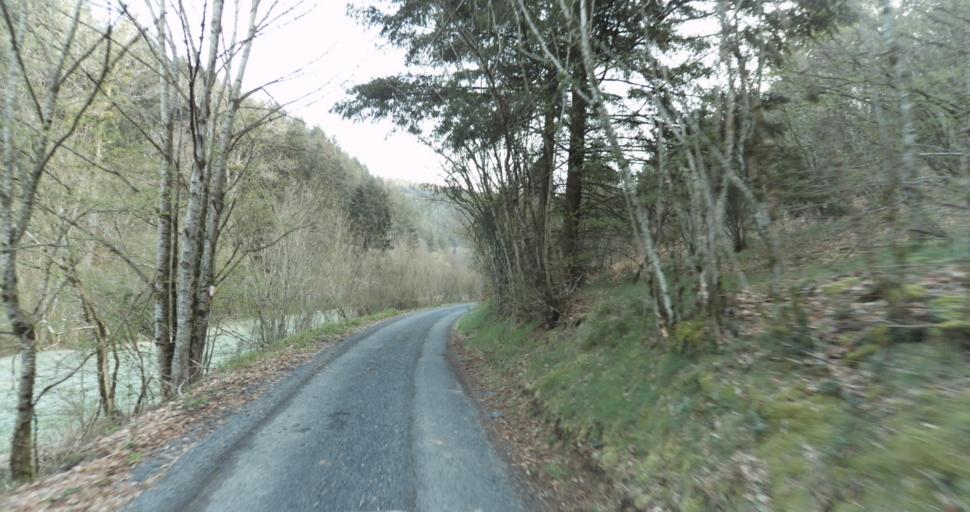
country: FR
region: Rhone-Alpes
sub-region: Departement du Rhone
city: Tarare
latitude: 45.9009
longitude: 4.4001
